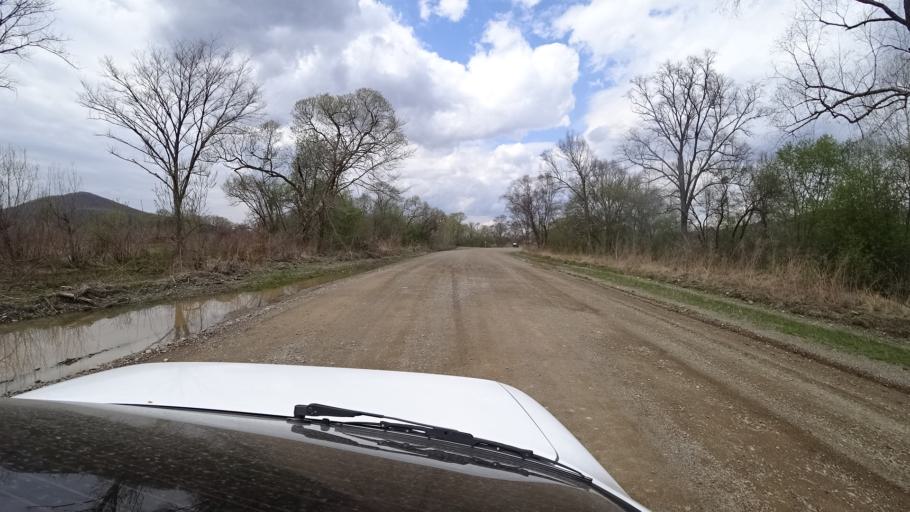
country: RU
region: Primorskiy
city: Novopokrovka
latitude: 45.6108
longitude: 134.2751
